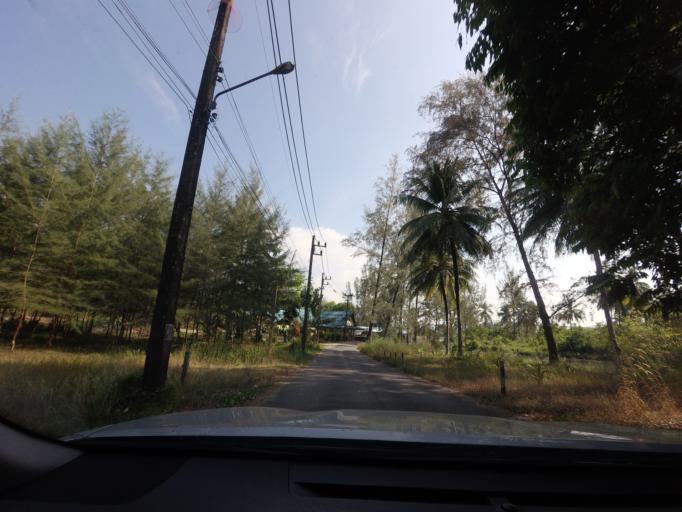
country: TH
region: Phangnga
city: Ban Khao Lak
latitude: 8.7337
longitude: 98.2425
